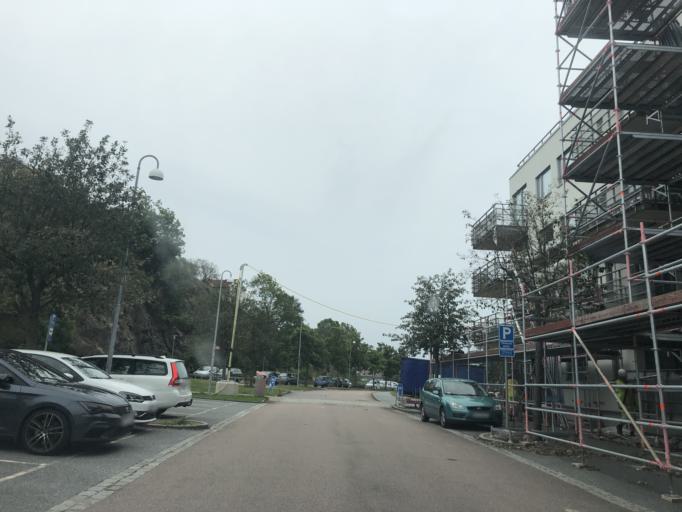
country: SE
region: Vaestra Goetaland
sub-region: Goteborg
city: Majorna
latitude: 57.7053
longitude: 11.9285
